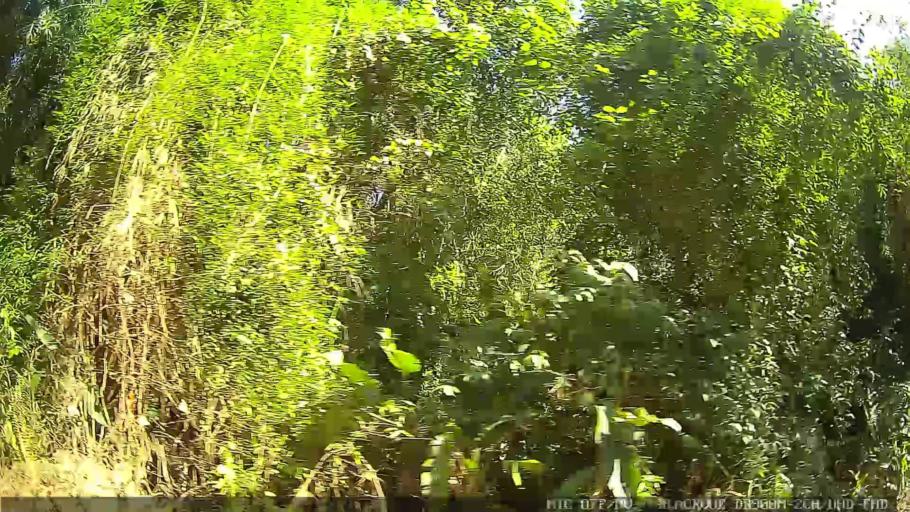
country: BR
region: Sao Paulo
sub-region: Santos
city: Santos
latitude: -24.0021
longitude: -46.3118
